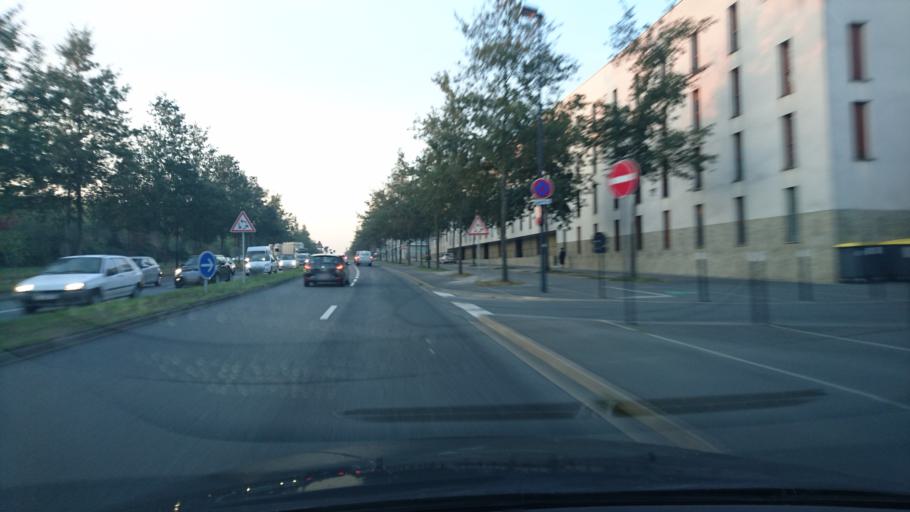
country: FR
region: Brittany
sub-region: Departement d'Ille-et-Vilaine
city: Saint-Jacques-de-la-Lande
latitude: 48.0797
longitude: -1.7128
